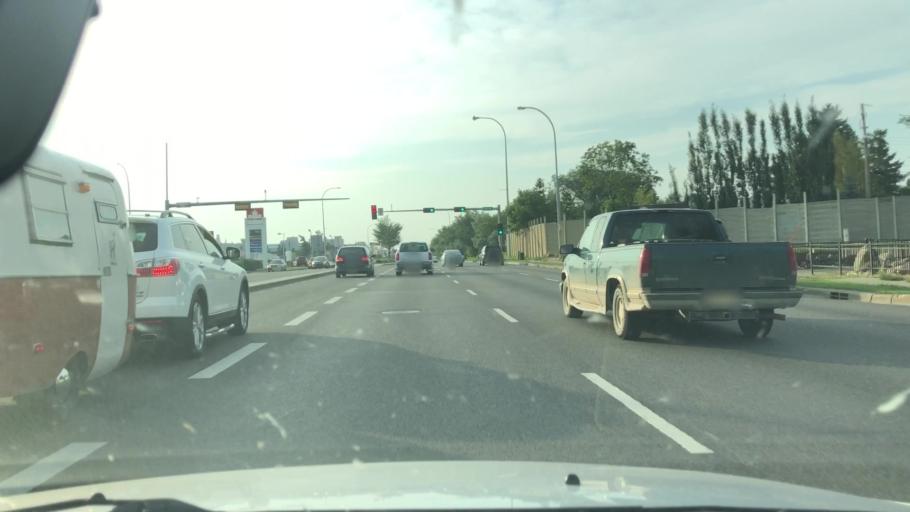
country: CA
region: Alberta
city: St. Albert
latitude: 53.6231
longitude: -113.6123
